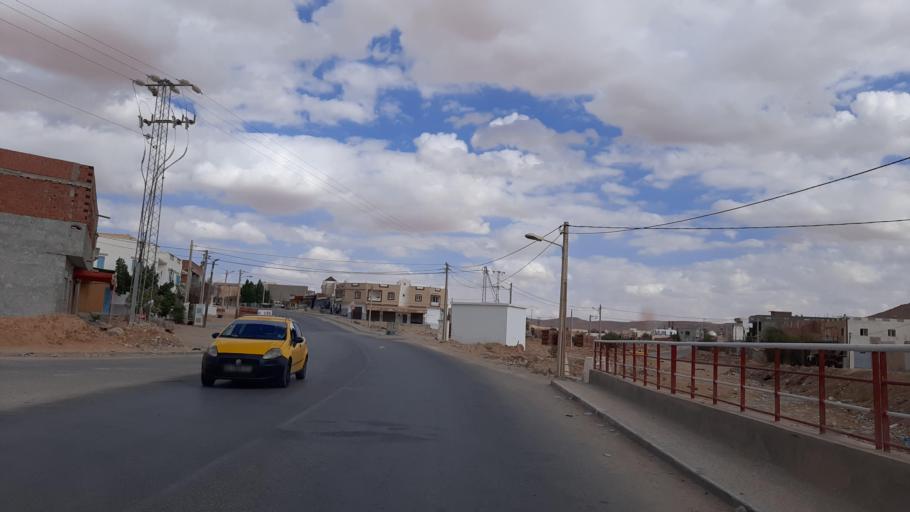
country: TN
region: Tataouine
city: Tataouine
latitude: 32.9189
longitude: 10.4672
